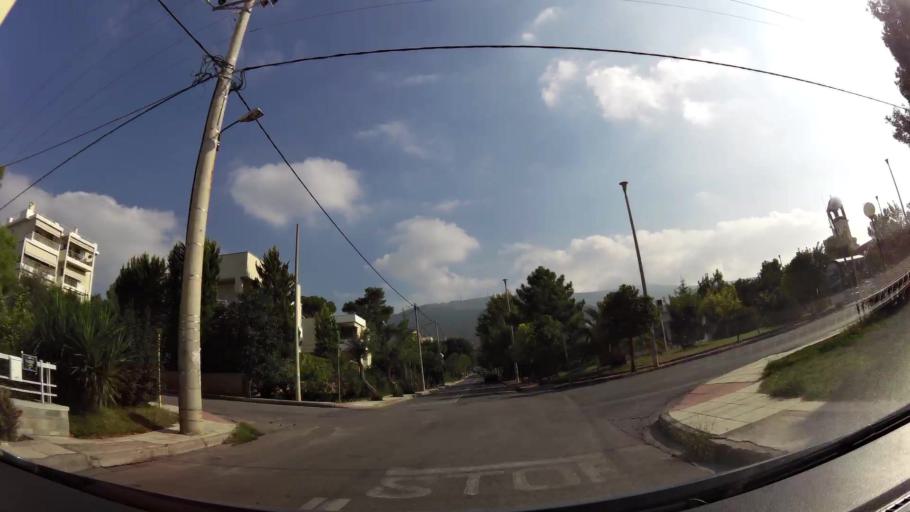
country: GR
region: Attica
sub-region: Nomarchia Athinas
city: Papagou
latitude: 37.9819
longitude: 23.7914
